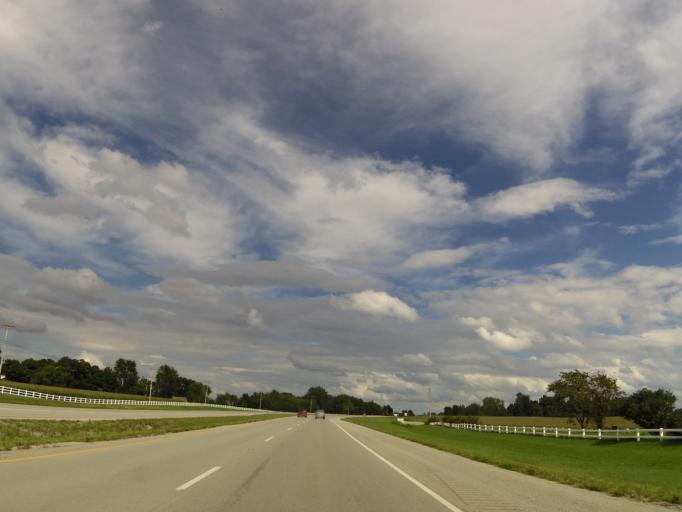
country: US
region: Kentucky
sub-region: Christian County
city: Hopkinsville
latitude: 36.8787
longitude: -87.5677
